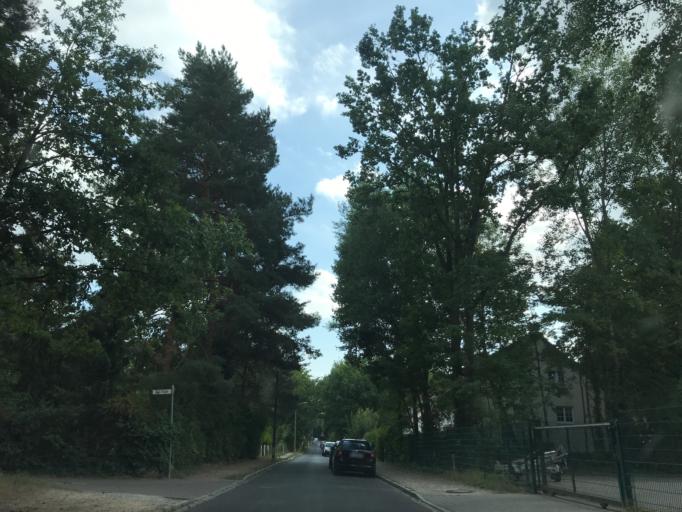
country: DE
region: Brandenburg
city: Kleinmachnow
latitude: 52.4130
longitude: 13.2305
